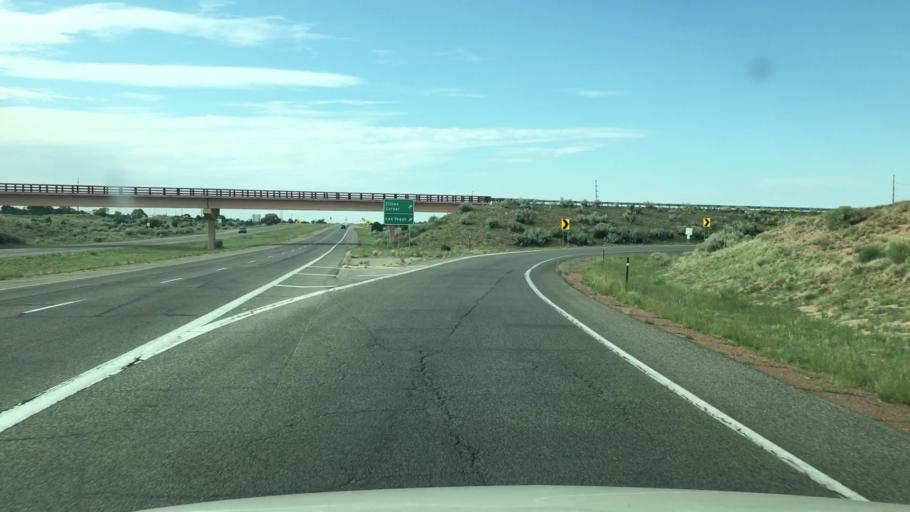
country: US
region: New Mexico
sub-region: Santa Fe County
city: Santa Fe
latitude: 35.6334
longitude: -105.9565
